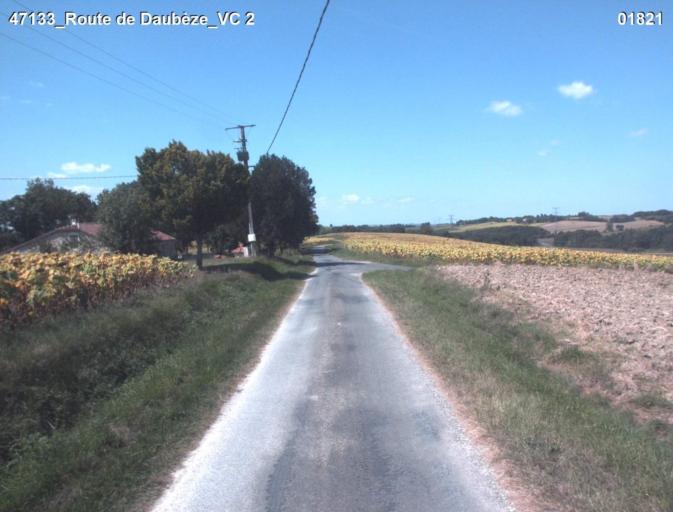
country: FR
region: Aquitaine
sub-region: Departement du Lot-et-Garonne
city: Laplume
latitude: 44.0798
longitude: 0.5544
